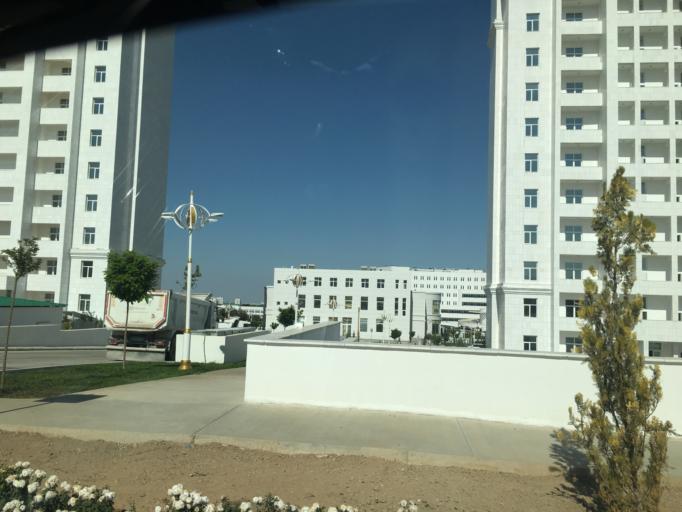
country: TM
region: Ahal
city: Ashgabat
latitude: 37.9382
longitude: 58.3604
